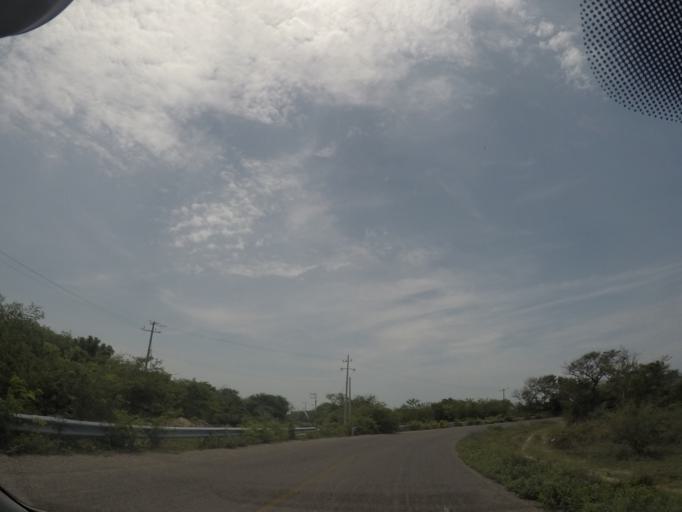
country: MX
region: Oaxaca
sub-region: San Mateo del Mar
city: Colonia Juarez
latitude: 16.2095
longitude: -95.0165
